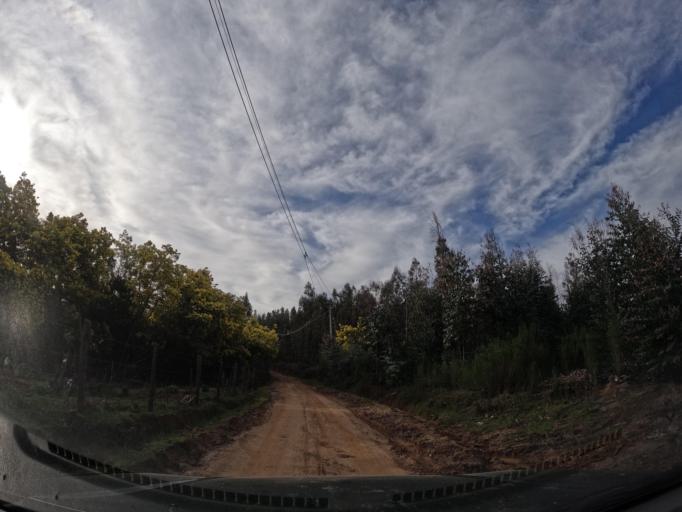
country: CL
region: Biobio
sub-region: Provincia de Concepcion
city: Chiguayante
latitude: -37.0349
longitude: -72.9046
